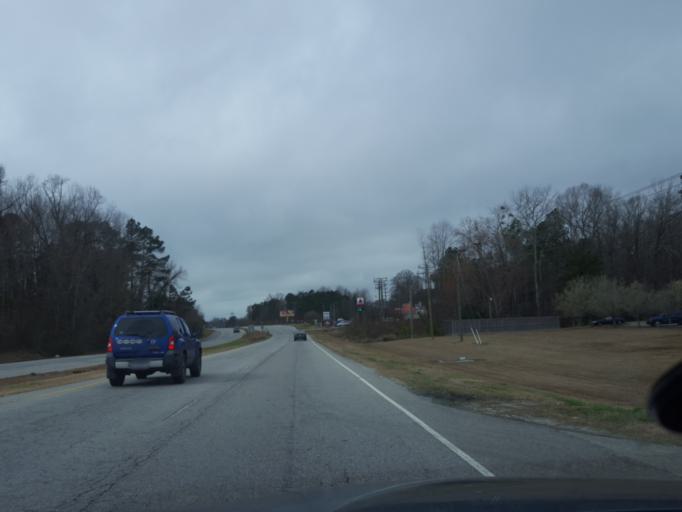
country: US
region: North Carolina
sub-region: Washington County
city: Plymouth
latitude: 35.8086
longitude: -76.8839
